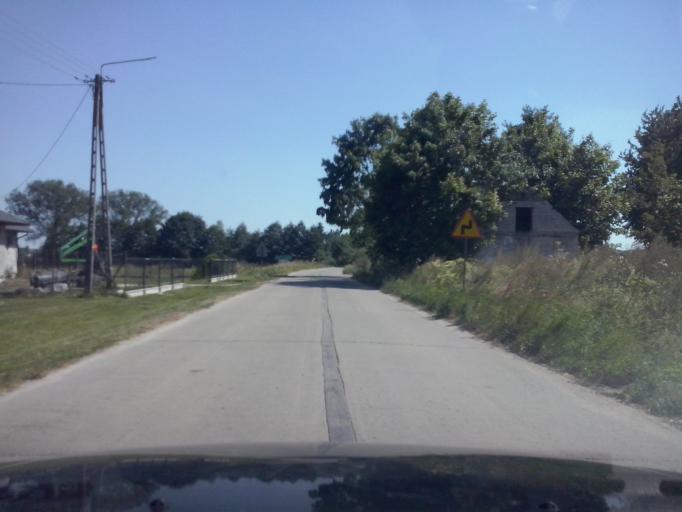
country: PL
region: Swietokrzyskie
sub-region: Powiat buski
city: Gnojno
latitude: 50.5965
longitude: 20.8130
